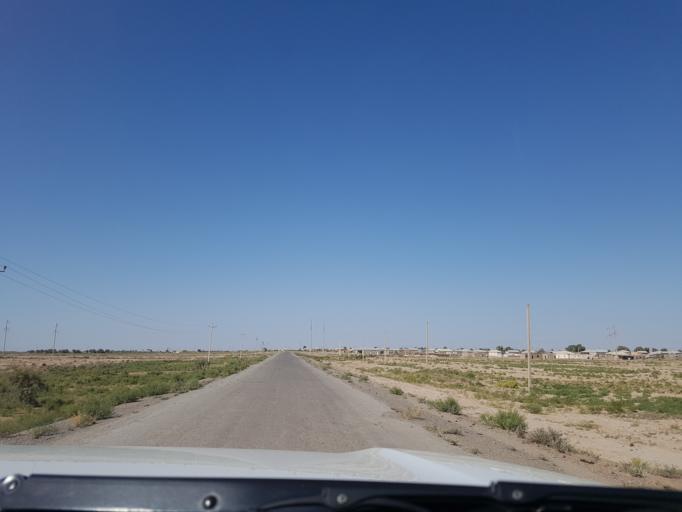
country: IR
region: Razavi Khorasan
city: Sarakhs
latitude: 36.5064
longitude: 61.2534
